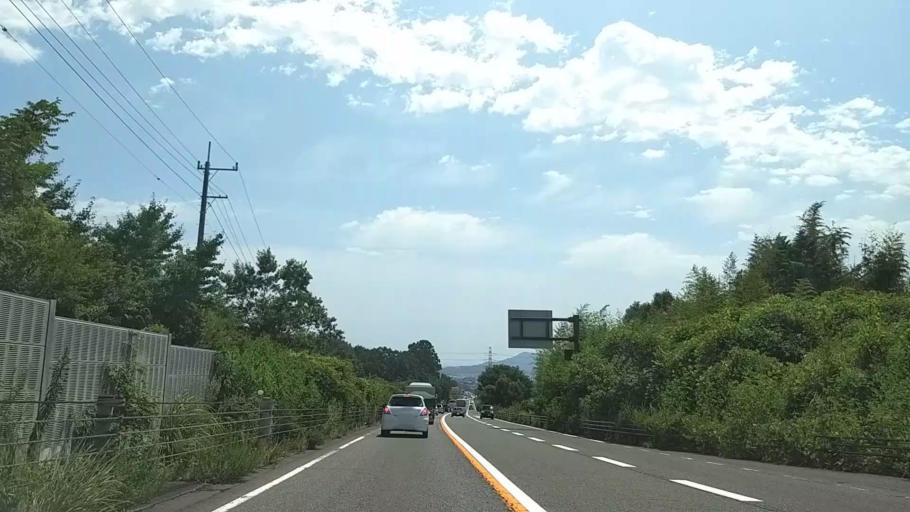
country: JP
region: Shizuoka
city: Fujinomiya
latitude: 35.2680
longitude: 138.6150
